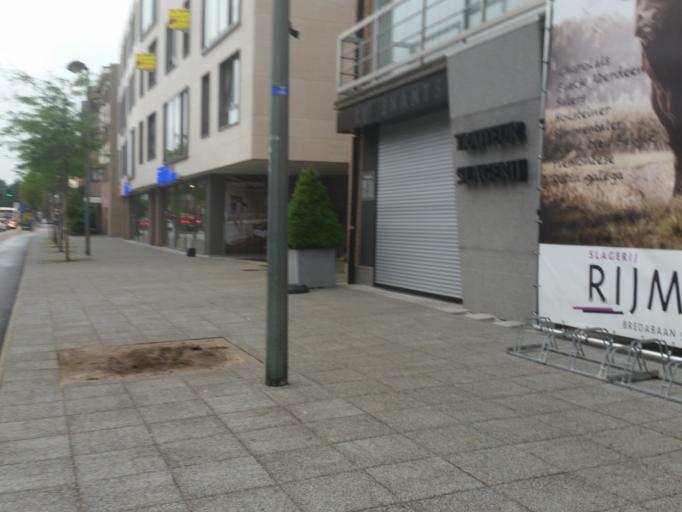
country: BE
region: Flanders
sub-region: Provincie Antwerpen
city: Brasschaat
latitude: 51.2952
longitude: 4.4968
